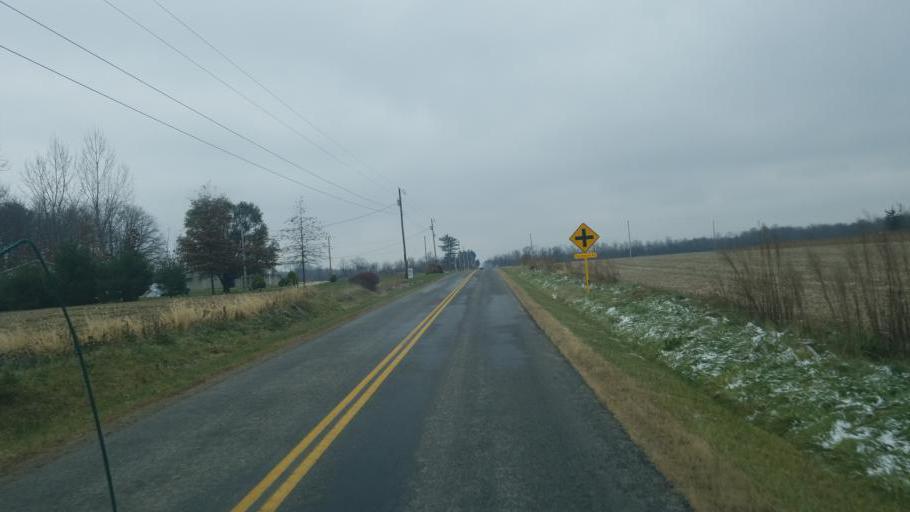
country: US
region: Ohio
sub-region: Medina County
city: Lodi
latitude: 41.1123
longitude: -82.0055
